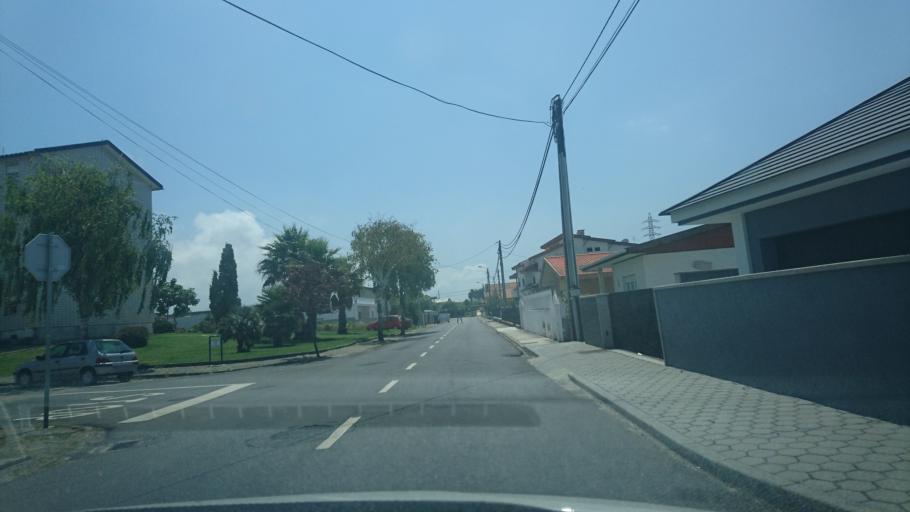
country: PT
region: Aveiro
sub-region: Ovar
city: Esmoriz
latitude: 40.9546
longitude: -8.6302
